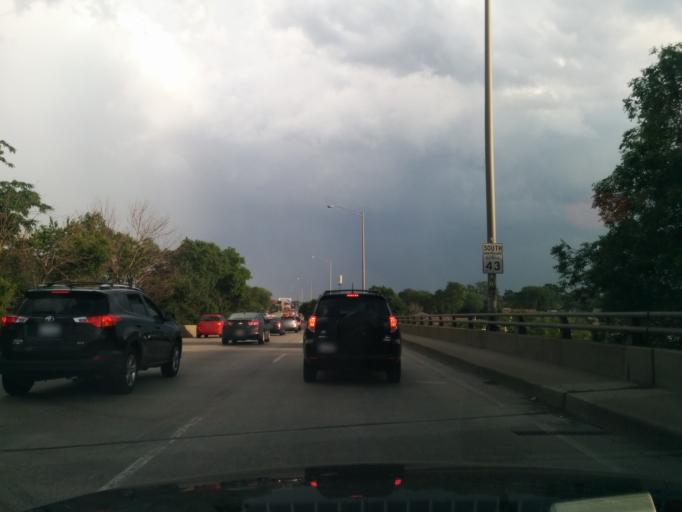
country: US
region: Illinois
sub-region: Cook County
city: Summit
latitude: 41.7978
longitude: -87.8021
